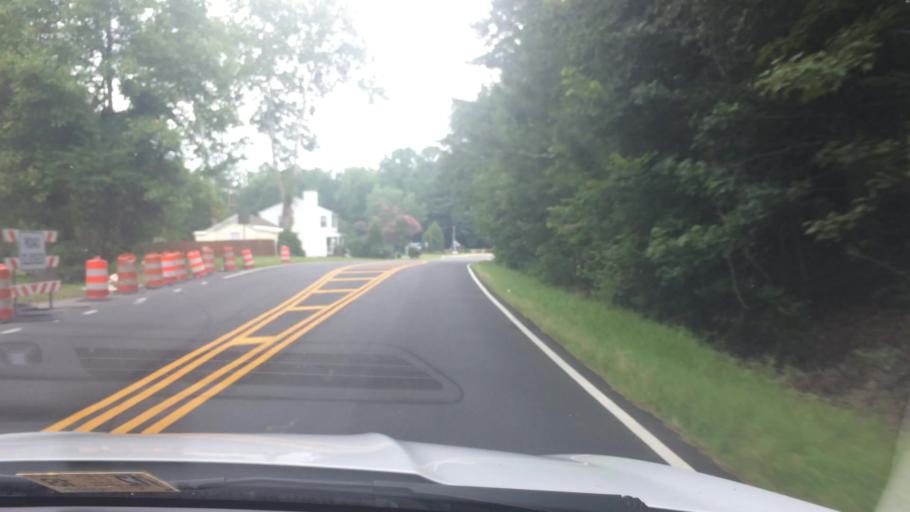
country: US
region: Virginia
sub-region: York County
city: Yorktown
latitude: 37.2247
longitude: -76.5200
